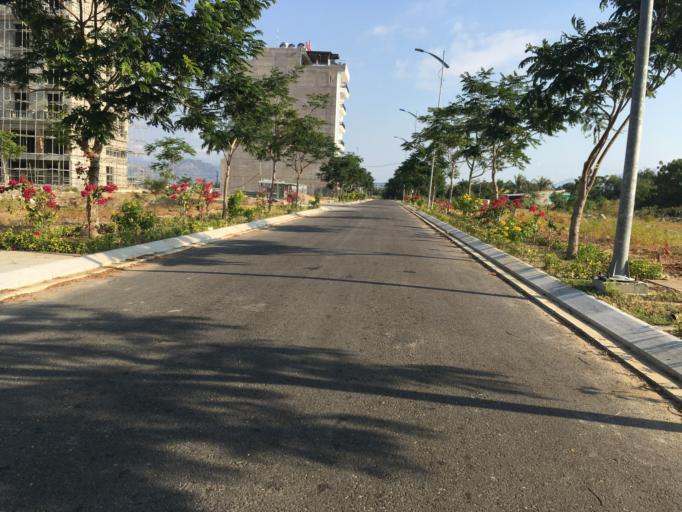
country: VN
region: Ninh Thuan
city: Phan Rang-Thap Cham
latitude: 11.5634
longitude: 109.0207
